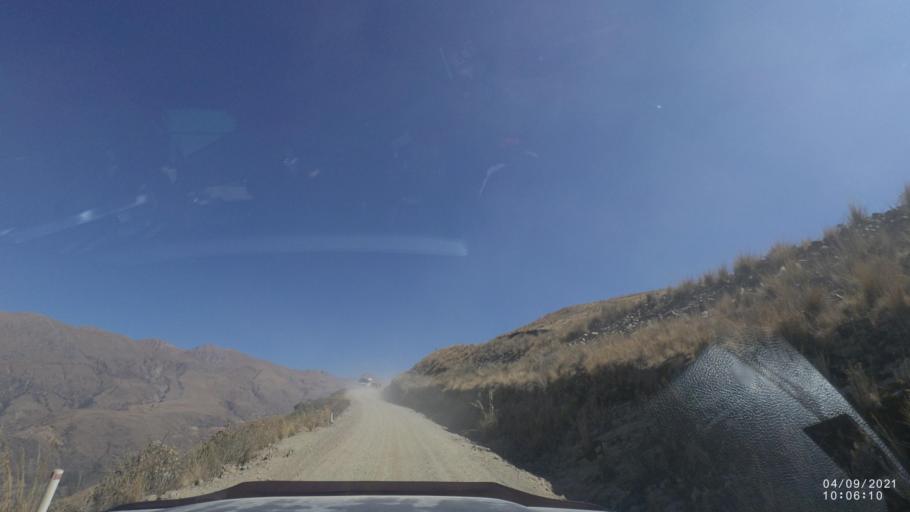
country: BO
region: Cochabamba
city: Sipe Sipe
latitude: -17.3521
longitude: -66.3909
